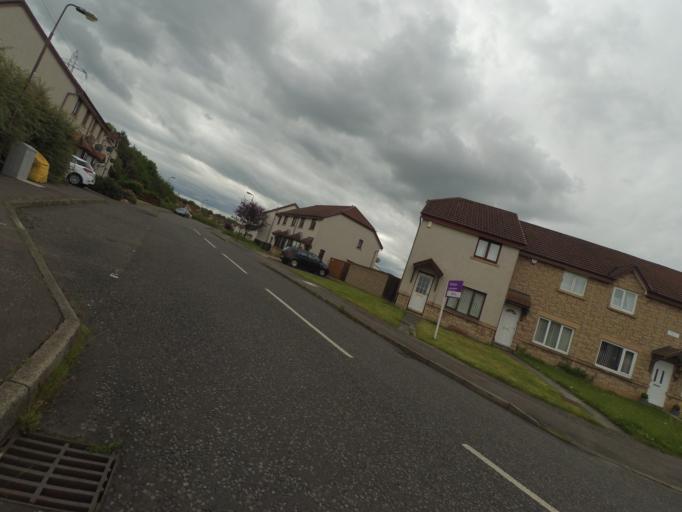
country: GB
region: Scotland
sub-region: East Lothian
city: Musselburgh
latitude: 55.9385
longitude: -3.0968
